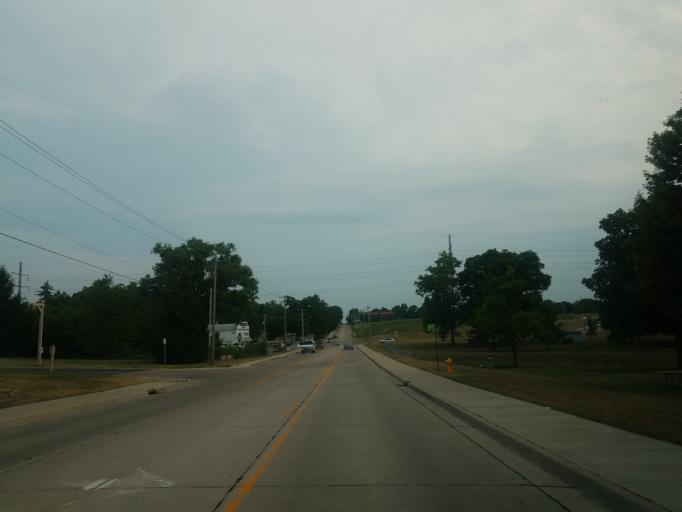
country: US
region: Illinois
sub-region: McLean County
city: Bloomington
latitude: 40.4628
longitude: -89.0060
